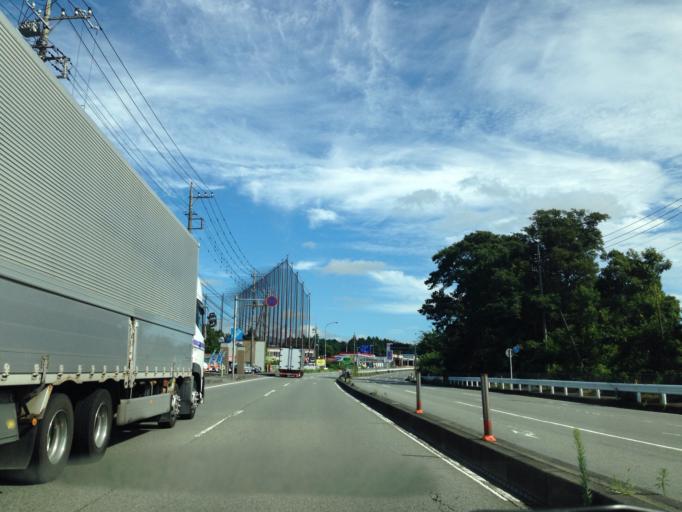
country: JP
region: Shizuoka
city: Gotemba
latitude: 35.2712
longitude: 138.9123
